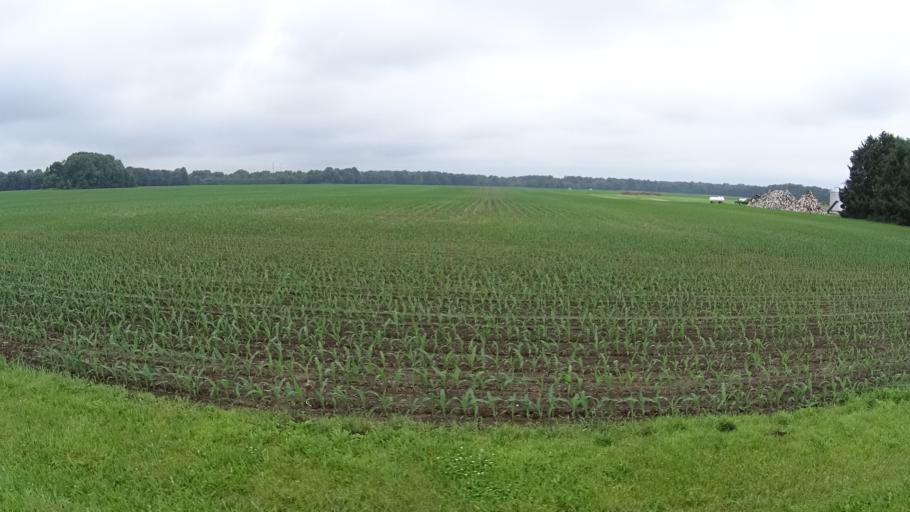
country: US
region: Ohio
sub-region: Erie County
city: Milan
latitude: 41.3111
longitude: -82.5431
